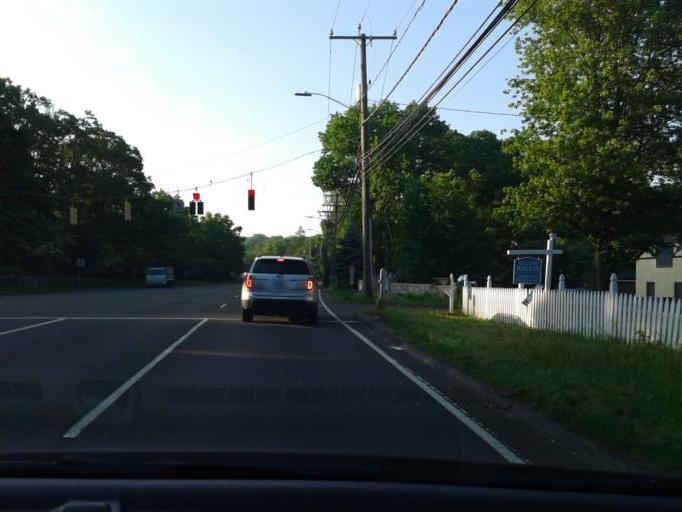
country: US
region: Connecticut
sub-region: Fairfield County
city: North Stamford
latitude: 41.0984
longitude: -73.5646
